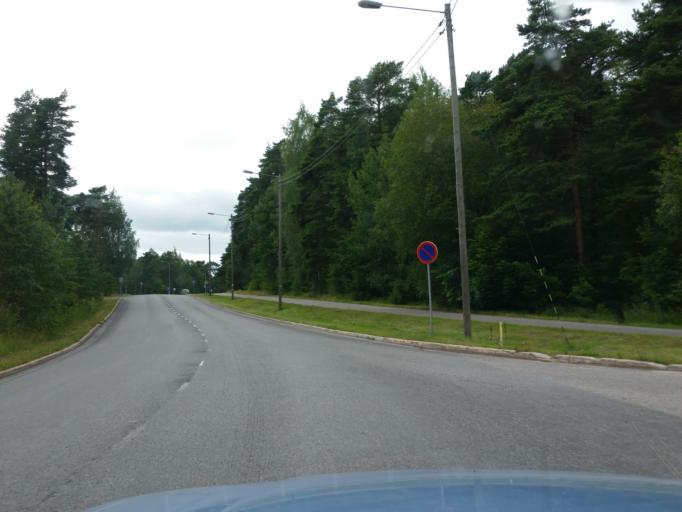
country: FI
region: Varsinais-Suomi
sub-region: Turku
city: Turku
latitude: 60.4368
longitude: 22.3092
